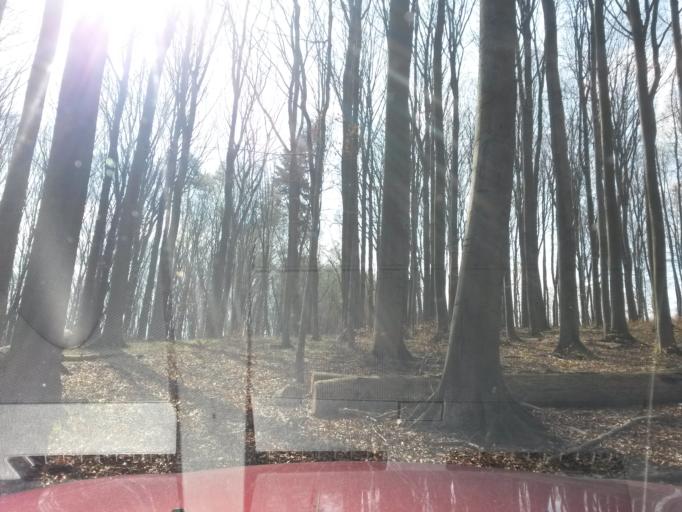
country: SK
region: Presovsky
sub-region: Okres Presov
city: Presov
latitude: 48.9362
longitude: 21.1468
